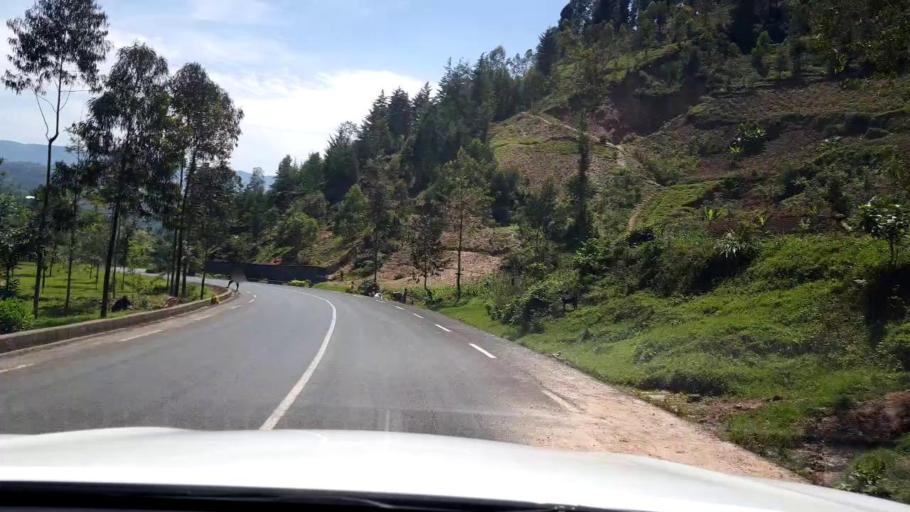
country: RW
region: Southern Province
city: Gitarama
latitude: -1.9188
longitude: 29.6323
